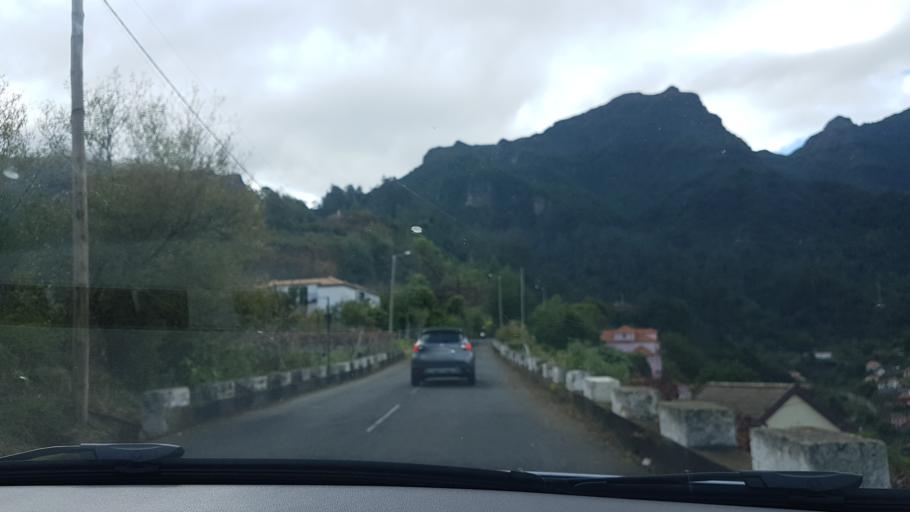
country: PT
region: Madeira
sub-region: Sao Vicente
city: Sao Vicente
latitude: 32.7755
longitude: -17.0274
